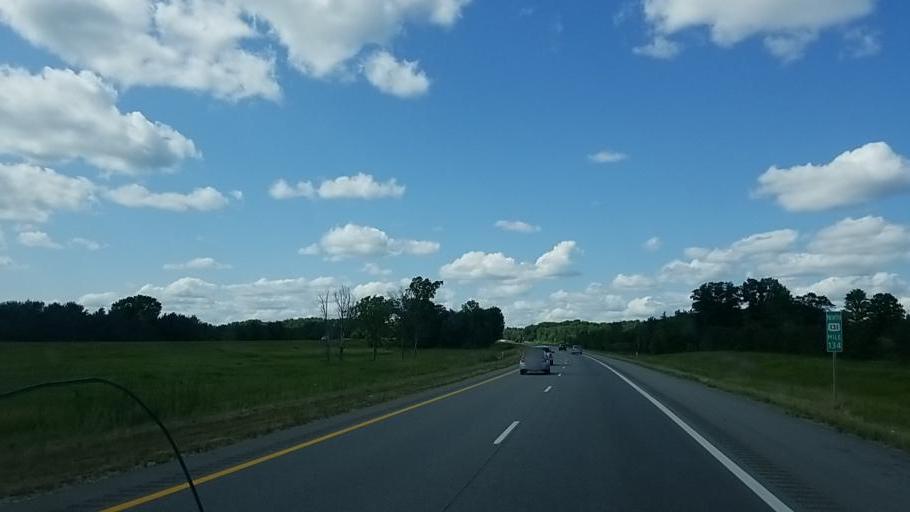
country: US
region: Michigan
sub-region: Mecosta County
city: Big Rapids
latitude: 43.6214
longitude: -85.4983
